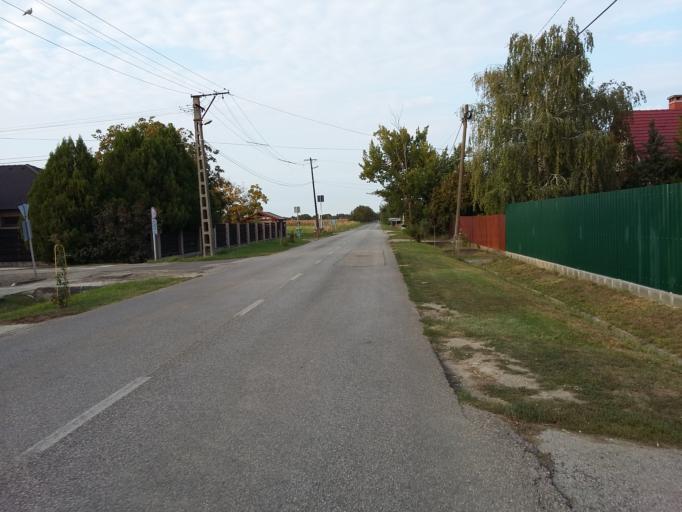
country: HU
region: Csongrad
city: Szeged
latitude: 46.2105
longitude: 20.1079
